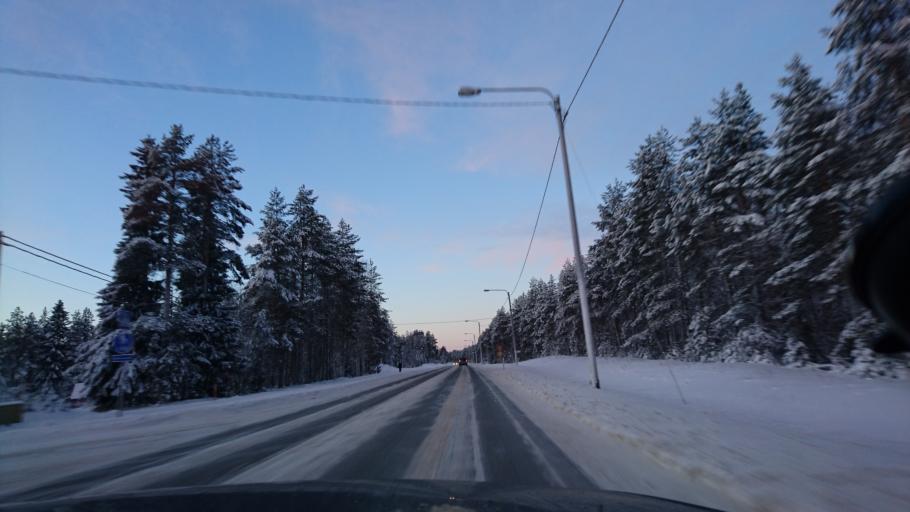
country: FI
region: Lapland
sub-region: Rovaniemi
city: Ranua
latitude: 65.9403
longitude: 26.4812
